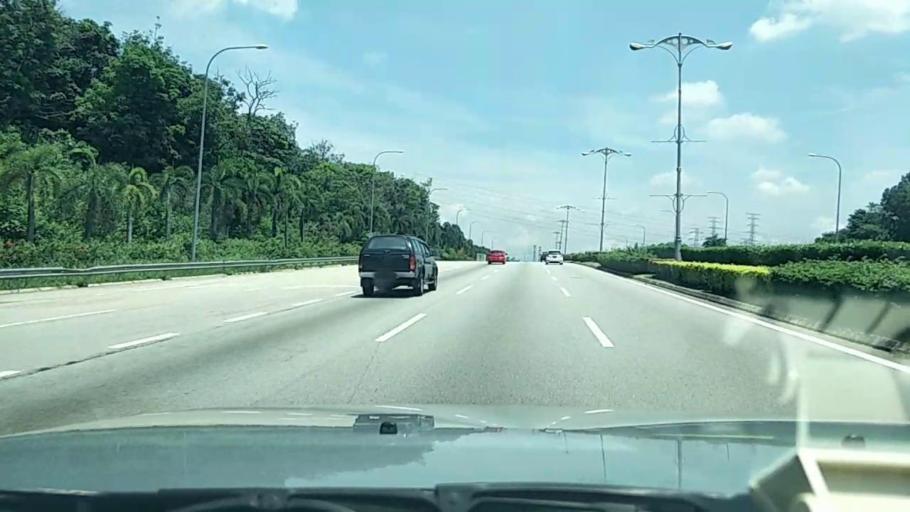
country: MY
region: Putrajaya
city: Putrajaya
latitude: 2.9635
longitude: 101.7187
